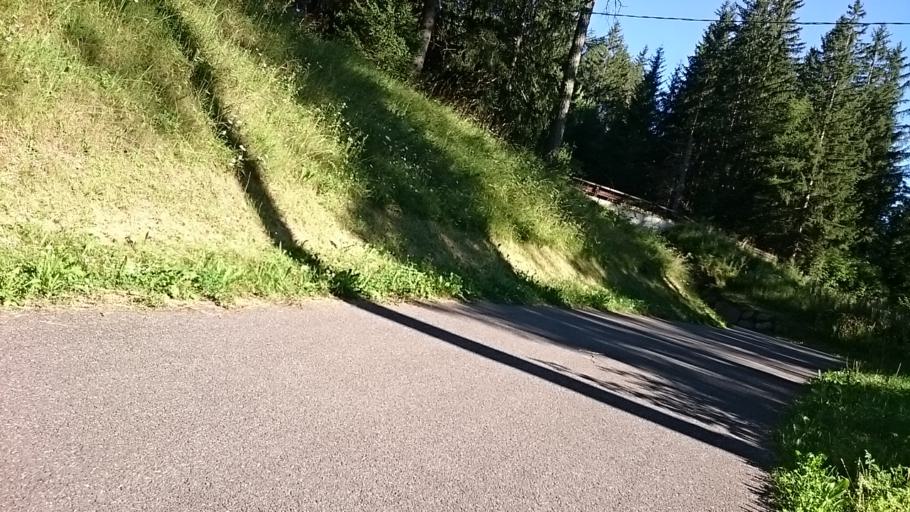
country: IT
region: Trentino-Alto Adige
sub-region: Bolzano
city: Braies
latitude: 46.7381
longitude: 12.1366
